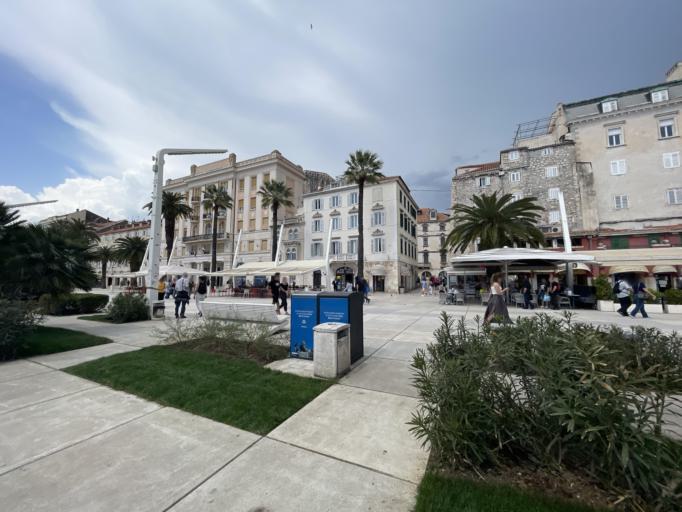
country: HR
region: Splitsko-Dalmatinska
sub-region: Grad Split
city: Split
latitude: 43.5076
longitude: 16.4385
